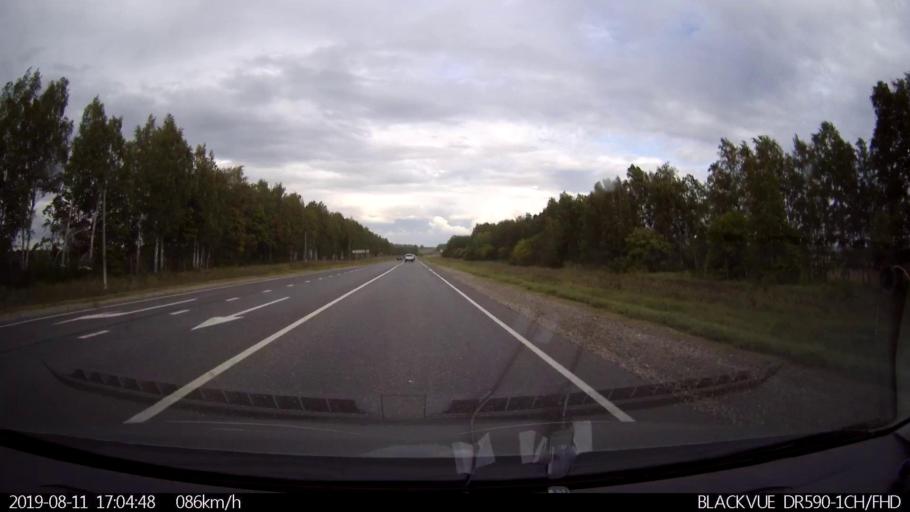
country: RU
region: Ulyanovsk
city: Mayna
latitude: 54.3000
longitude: 47.7715
